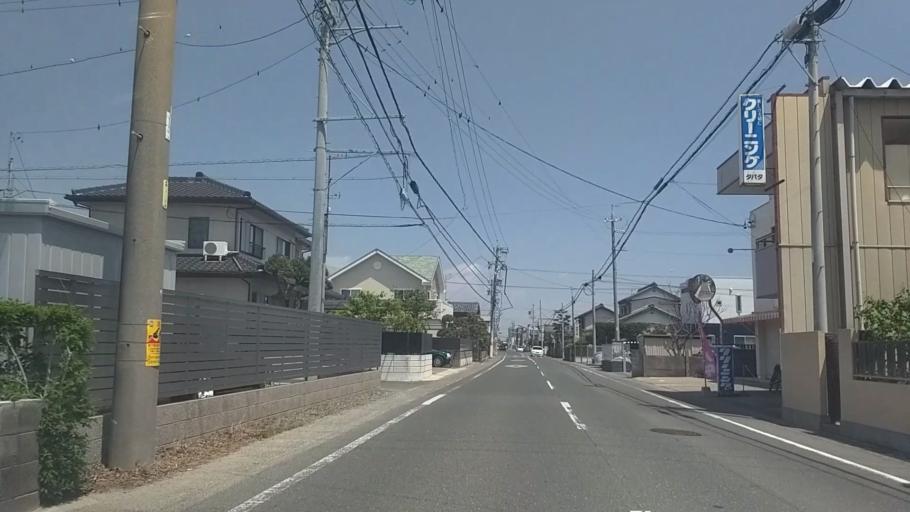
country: JP
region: Shizuoka
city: Hamamatsu
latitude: 34.6860
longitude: 137.6651
